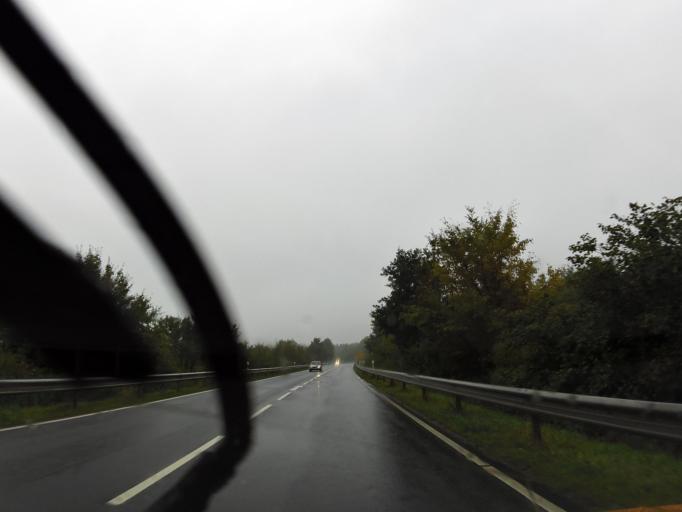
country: DE
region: Lower Saxony
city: Bad Sachsa
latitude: 51.5893
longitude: 10.5473
